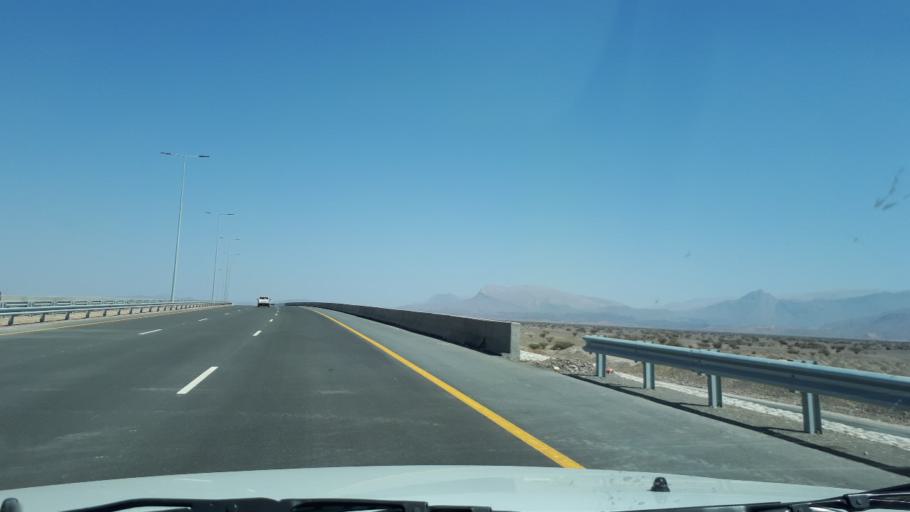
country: OM
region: Ash Sharqiyah
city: Badiyah
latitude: 22.3581
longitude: 59.1137
